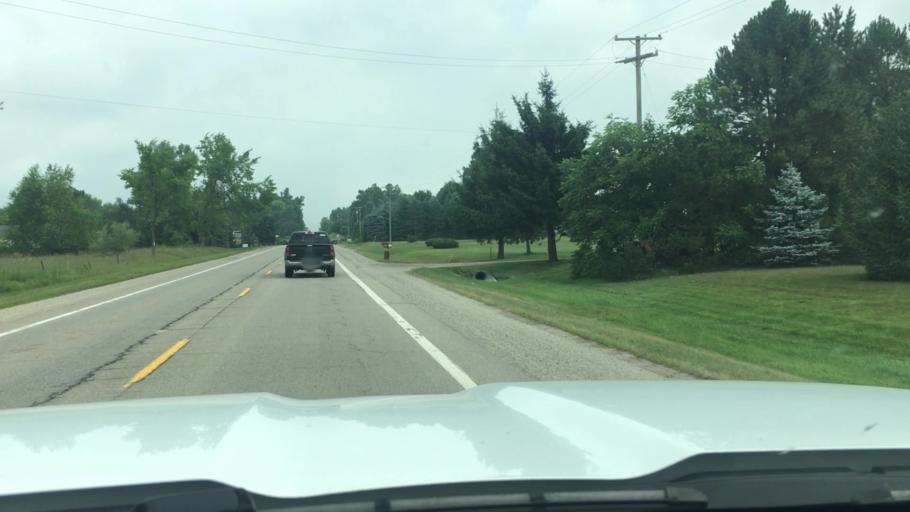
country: US
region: Michigan
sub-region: Sanilac County
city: Brown City
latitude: 43.1577
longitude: -83.0754
